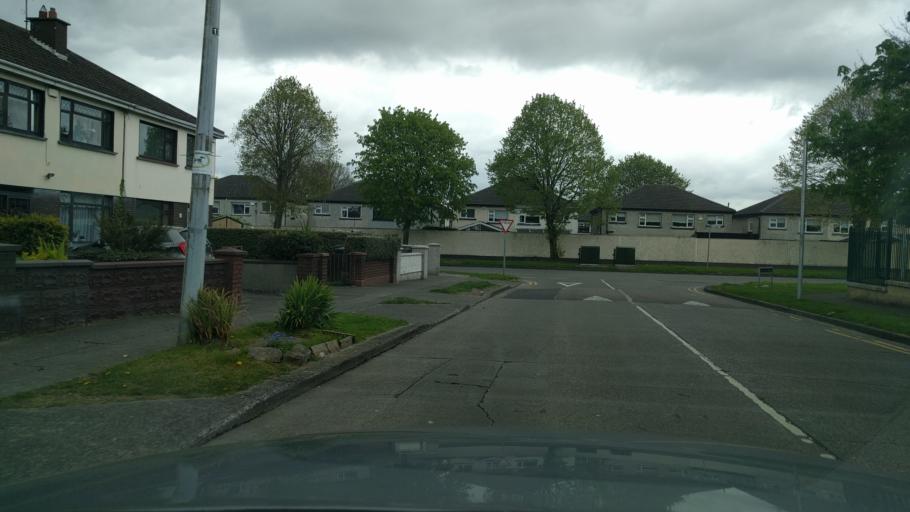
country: IE
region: Leinster
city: Tallaght
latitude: 53.3072
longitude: -6.3700
